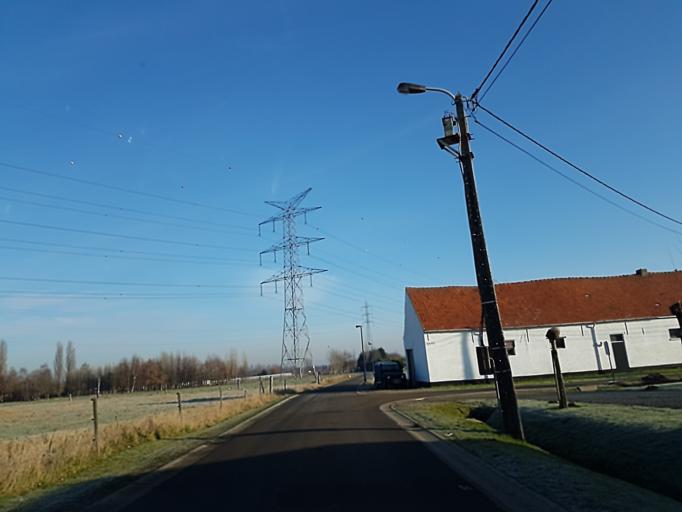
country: BE
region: Flanders
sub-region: Provincie Antwerpen
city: Kontich
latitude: 51.1136
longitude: 4.4594
